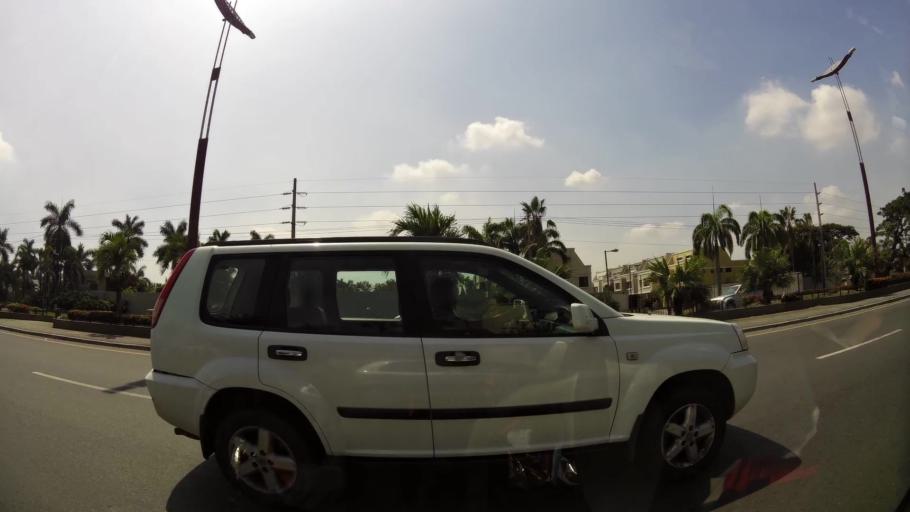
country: EC
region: Guayas
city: Eloy Alfaro
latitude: -2.1214
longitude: -79.8659
